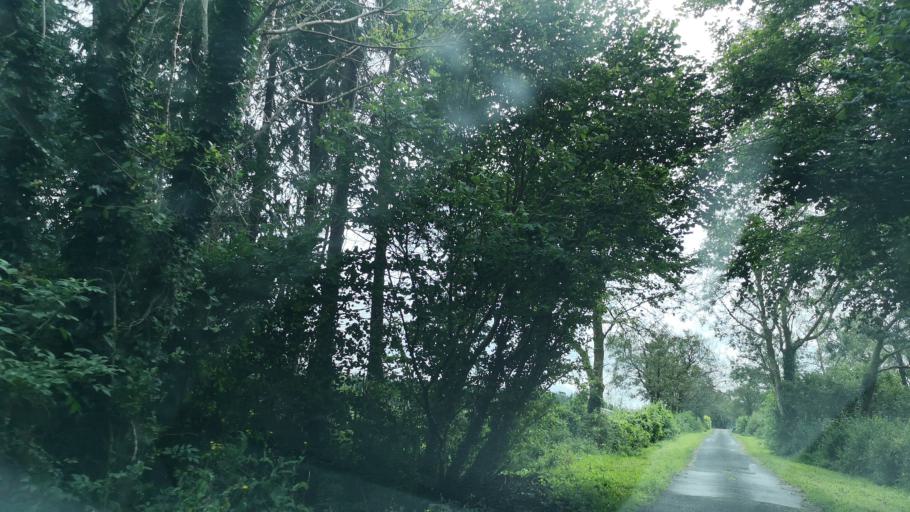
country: IE
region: Connaught
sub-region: County Galway
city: Athenry
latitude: 53.2937
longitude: -8.6632
